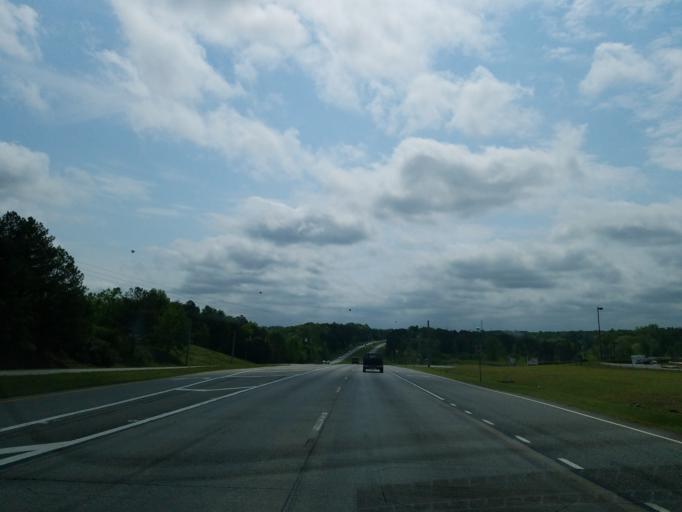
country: US
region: Georgia
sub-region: Pickens County
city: Jasper
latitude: 34.4475
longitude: -84.4467
